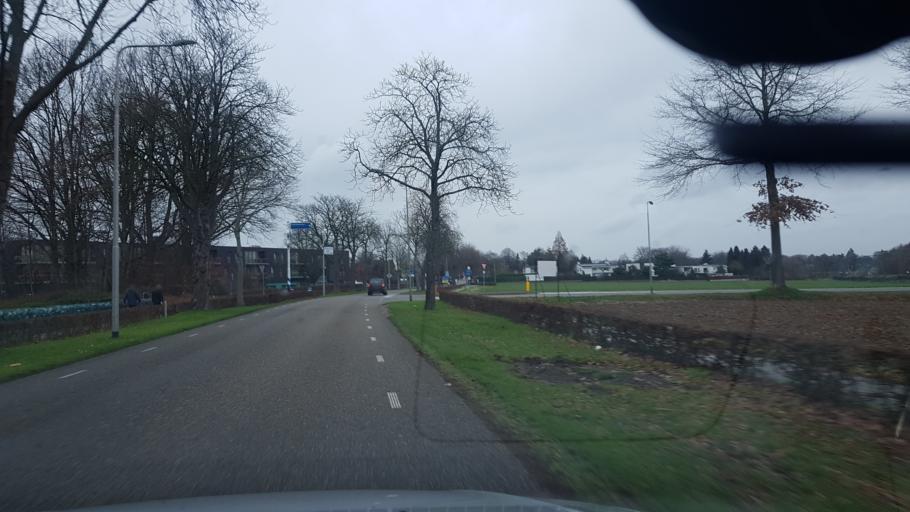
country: NL
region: Limburg
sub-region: Gemeente Schinnen
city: Puth
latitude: 50.9526
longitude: 5.8350
